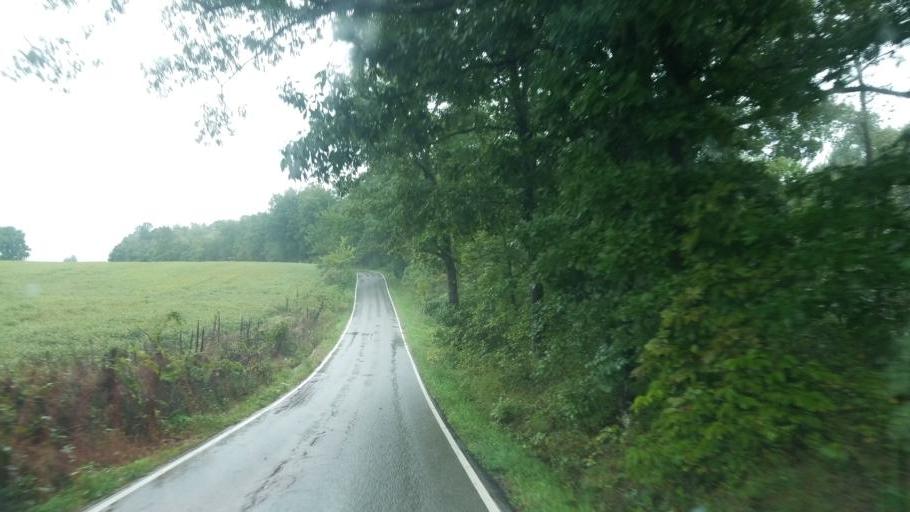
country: US
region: Kentucky
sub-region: Fleming County
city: Flemingsburg
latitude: 38.4761
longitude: -83.5118
